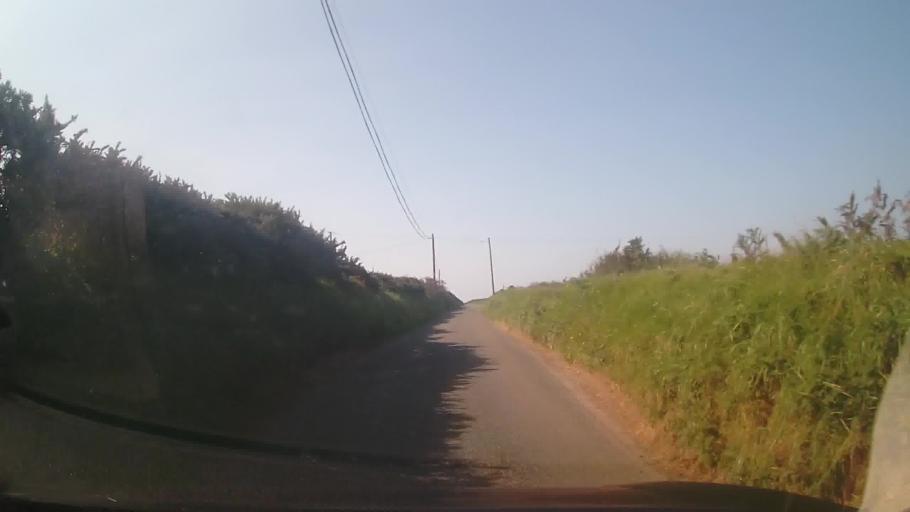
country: GB
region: Wales
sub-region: Pembrokeshire
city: Llanrhian
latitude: 51.9283
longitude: -5.1684
